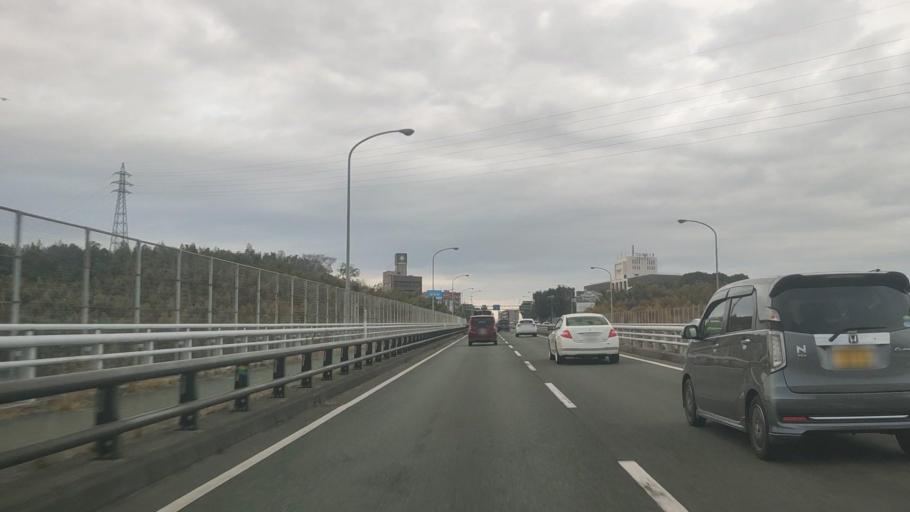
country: JP
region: Kumamoto
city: Ozu
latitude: 32.8483
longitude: 130.7821
